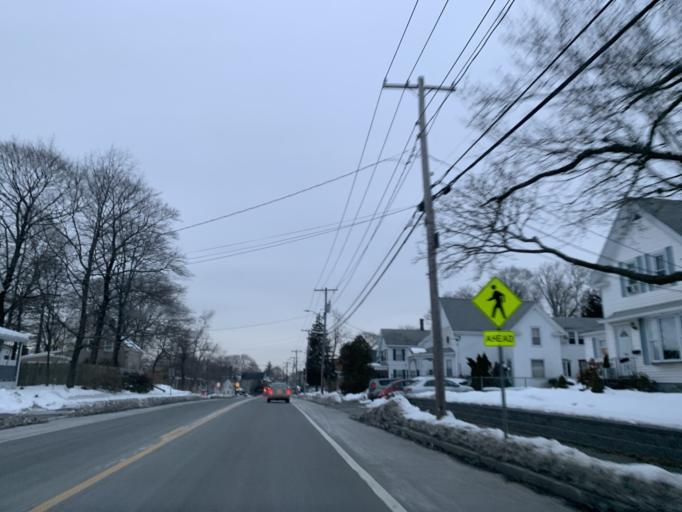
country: US
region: Massachusetts
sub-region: Norfolk County
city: Stoughton
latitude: 42.1214
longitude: -71.0952
